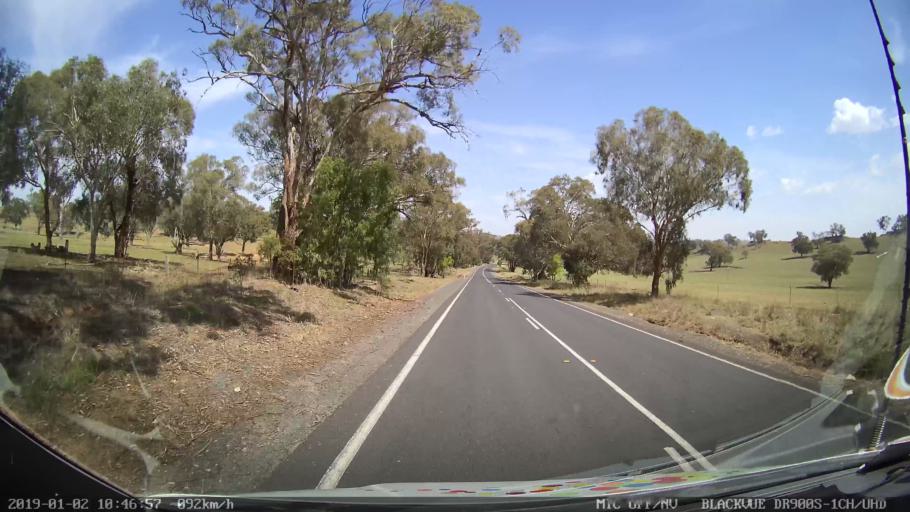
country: AU
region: New South Wales
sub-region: Cootamundra
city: Cootamundra
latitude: -34.7493
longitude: 148.2795
